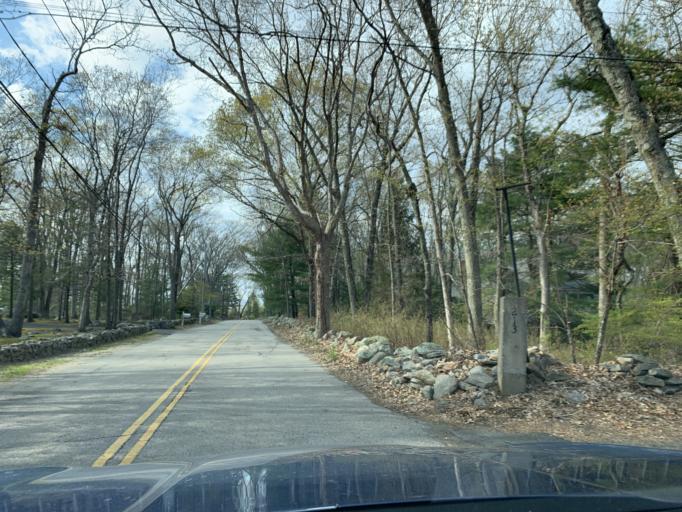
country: US
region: Rhode Island
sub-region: Washington County
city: Exeter
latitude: 41.5994
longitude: -71.5211
